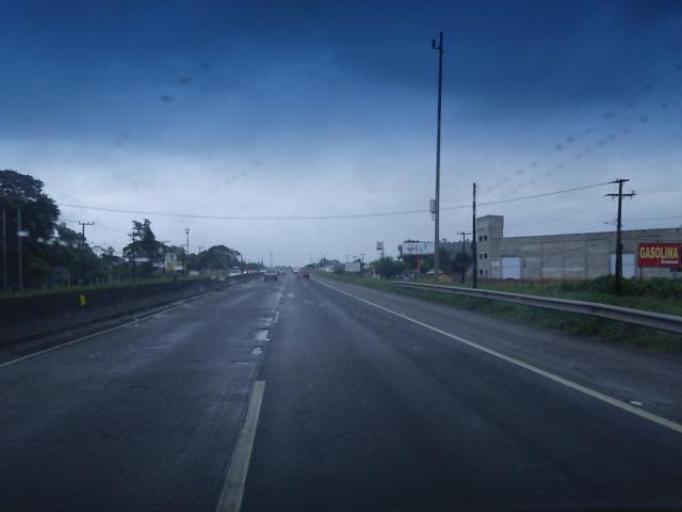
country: BR
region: Santa Catarina
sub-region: Barra Velha
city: Barra Velha
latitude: -26.5328
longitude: -48.7139
